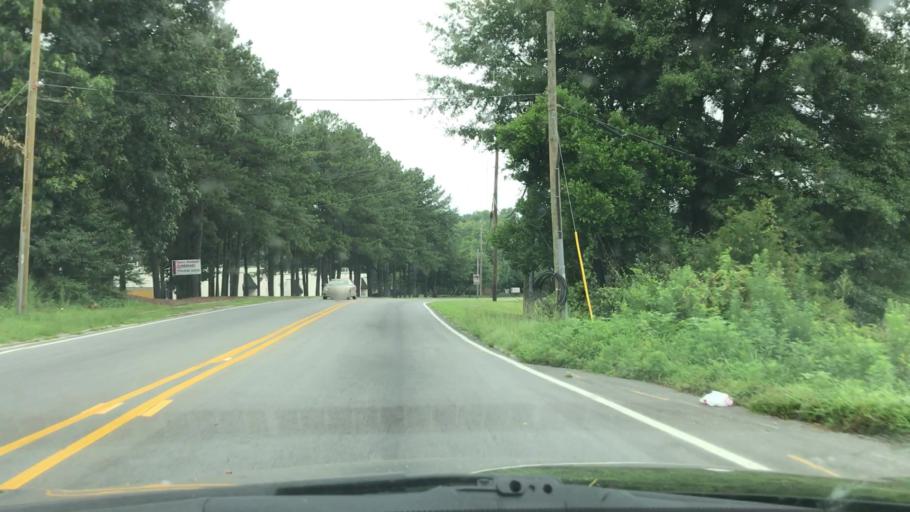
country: US
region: Georgia
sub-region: DeKalb County
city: Doraville
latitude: 33.9017
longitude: -84.2519
